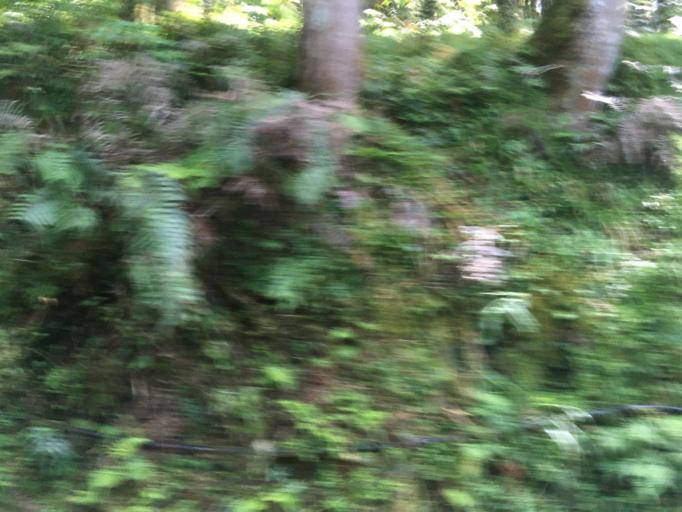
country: TW
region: Taiwan
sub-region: Yilan
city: Yilan
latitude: 24.6186
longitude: 121.4813
